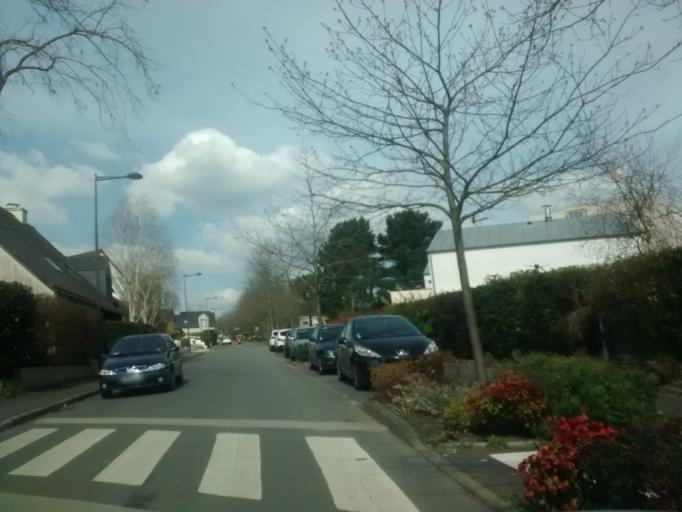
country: FR
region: Brittany
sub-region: Departement d'Ille-et-Vilaine
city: Chantepie
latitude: 48.0830
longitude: -1.6120
